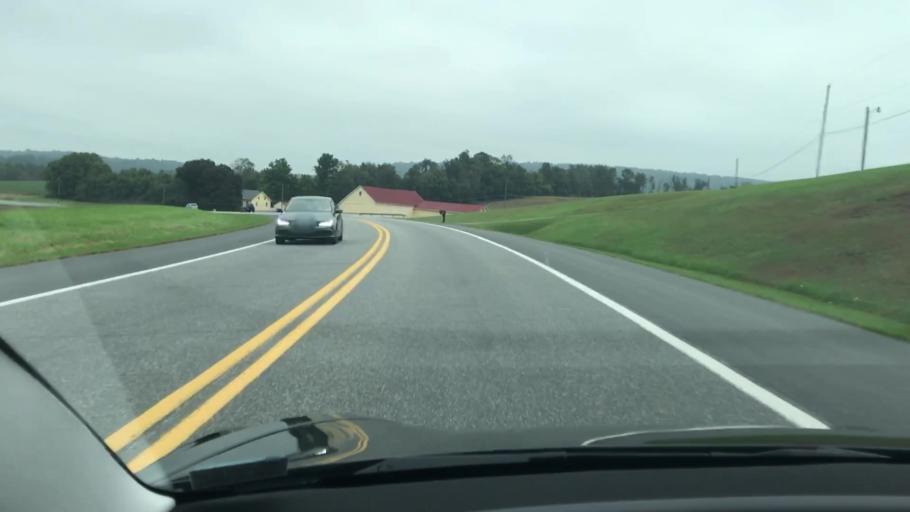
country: US
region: Pennsylvania
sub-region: Cumberland County
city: Lower Allen
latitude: 40.1495
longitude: -76.8835
